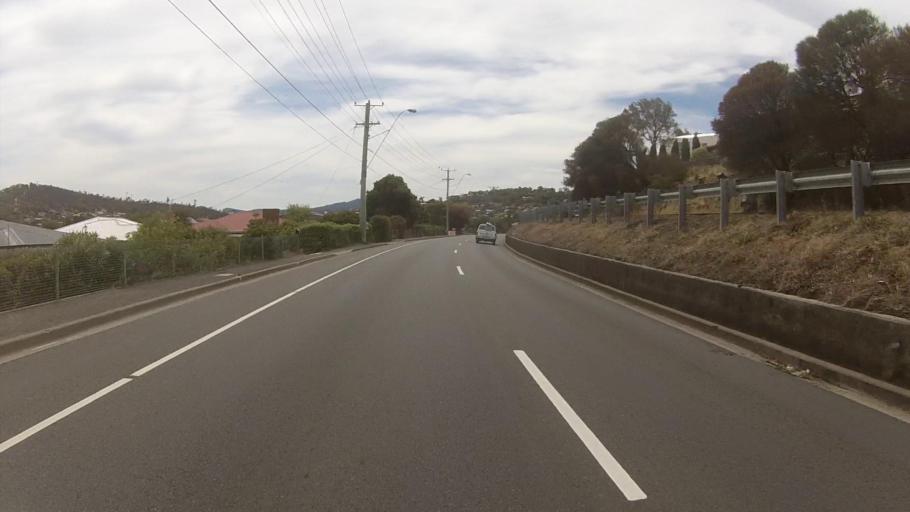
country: AU
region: Tasmania
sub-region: Clarence
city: Lindisfarne
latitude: -42.8552
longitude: 147.3567
